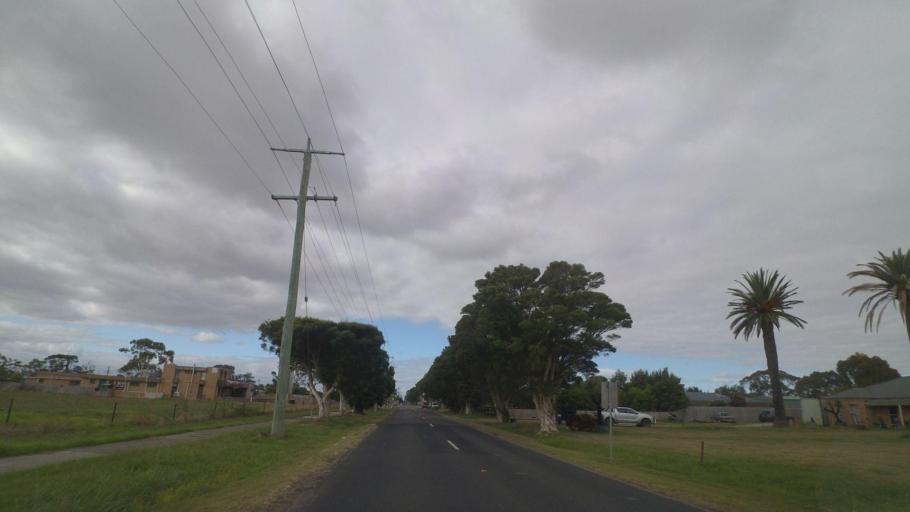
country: AU
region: Victoria
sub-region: Cardinia
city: Pakenham South
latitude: -38.0796
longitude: 145.5706
